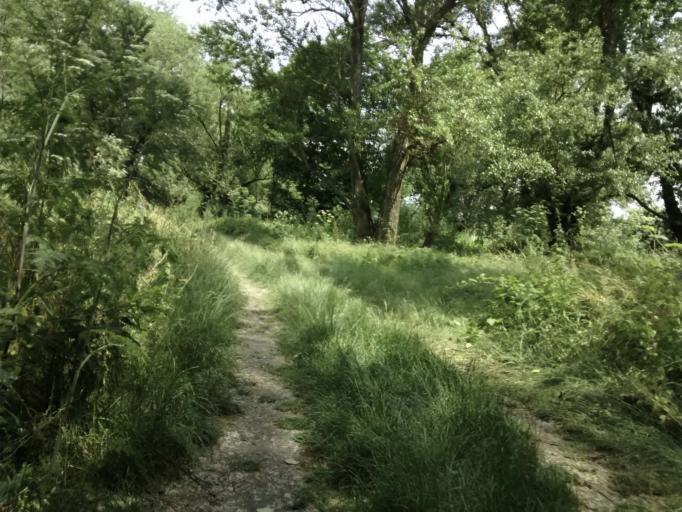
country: DE
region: Saxony-Anhalt
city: Neue Neustadt
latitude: 52.1515
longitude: 11.6679
